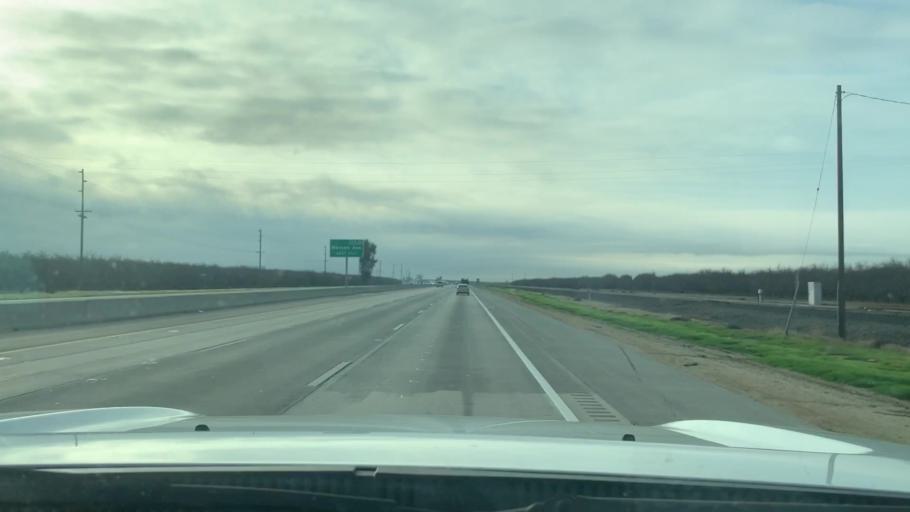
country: US
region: California
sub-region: Kern County
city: Shafter
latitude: 35.5446
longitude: -119.1950
